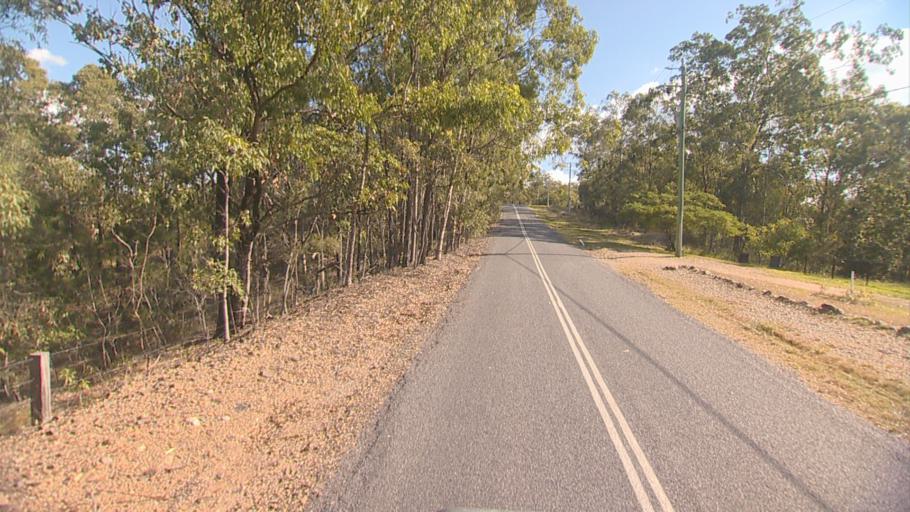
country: AU
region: Queensland
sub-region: Logan
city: Windaroo
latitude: -27.7388
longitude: 153.1620
